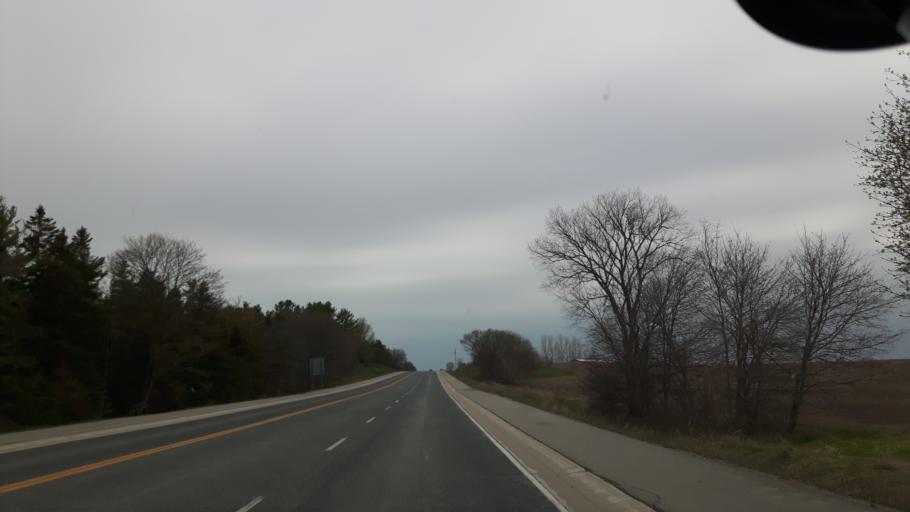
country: CA
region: Ontario
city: Goderich
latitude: 43.6482
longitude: -81.6041
